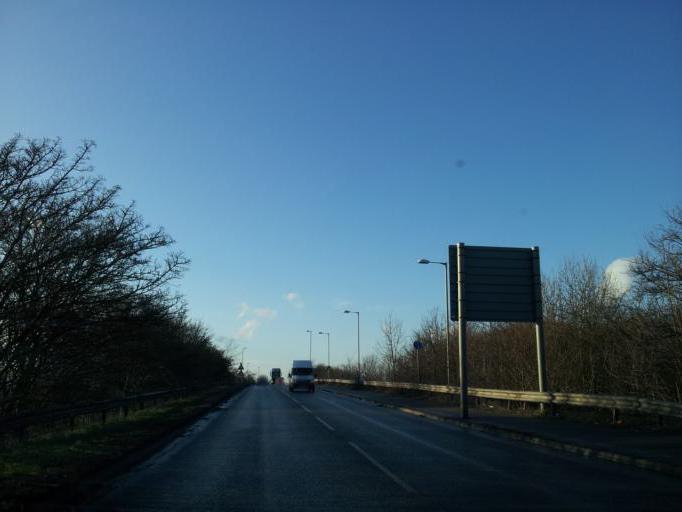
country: GB
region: England
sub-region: Nottinghamshire
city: Newark on Trent
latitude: 53.0457
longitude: -0.7757
